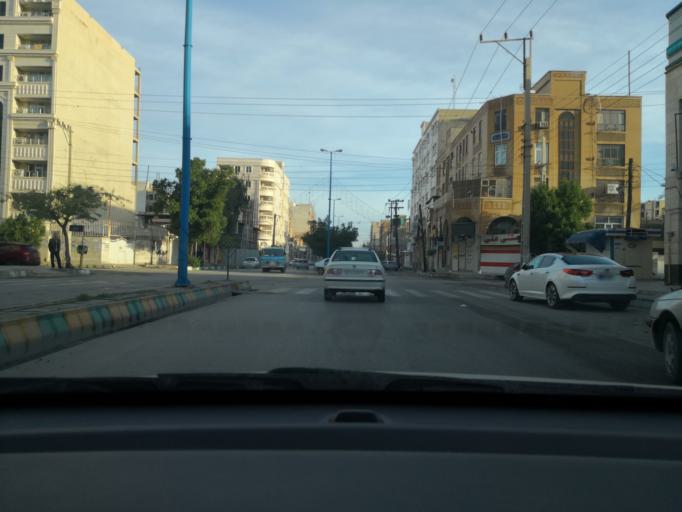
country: IR
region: Khuzestan
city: Ahvaz
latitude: 31.3533
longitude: 48.6775
